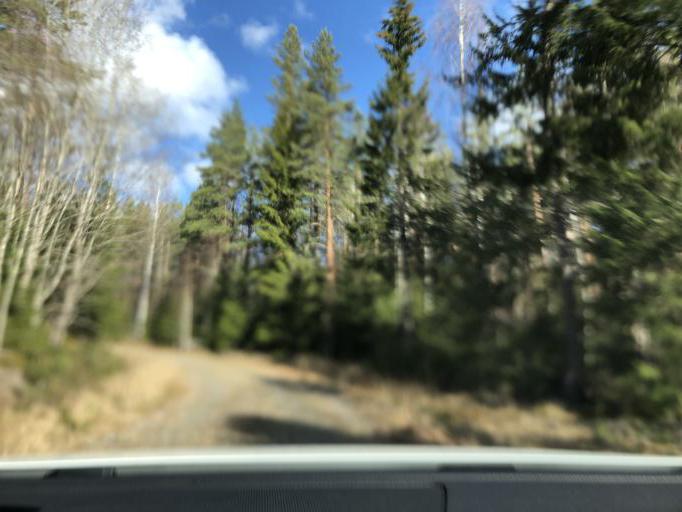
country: SE
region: Uppsala
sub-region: Heby Kommun
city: Tarnsjo
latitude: 60.3002
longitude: 16.8510
